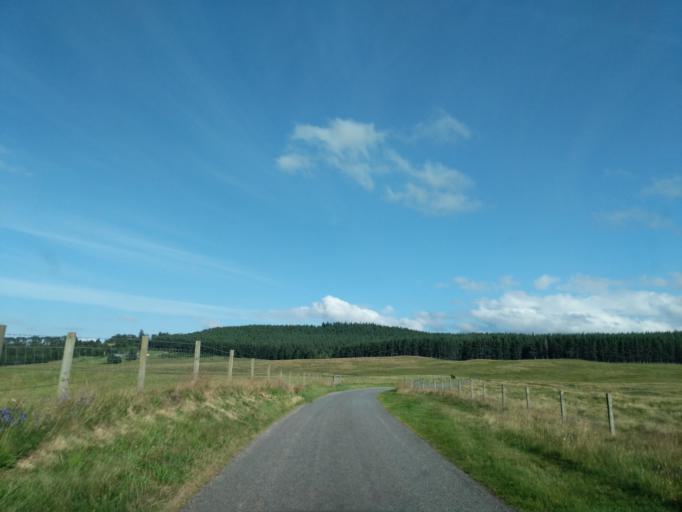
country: GB
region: Scotland
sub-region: Highland
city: Grantown on Spey
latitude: 57.2892
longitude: -3.7308
